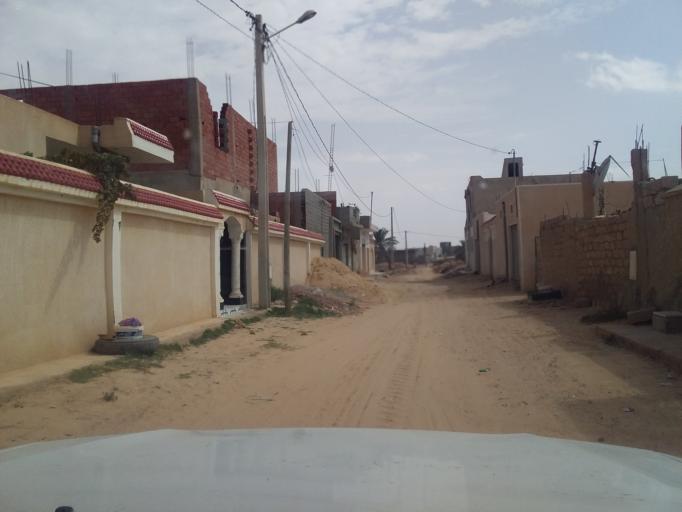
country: TN
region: Qabis
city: Matmata
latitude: 33.6151
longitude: 10.2760
